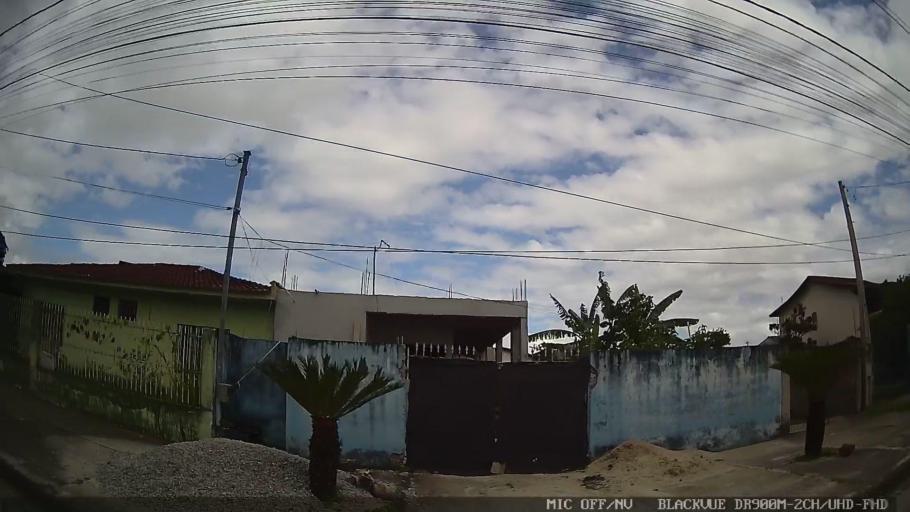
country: BR
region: Sao Paulo
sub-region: Caraguatatuba
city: Caraguatatuba
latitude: -23.6431
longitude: -45.4420
